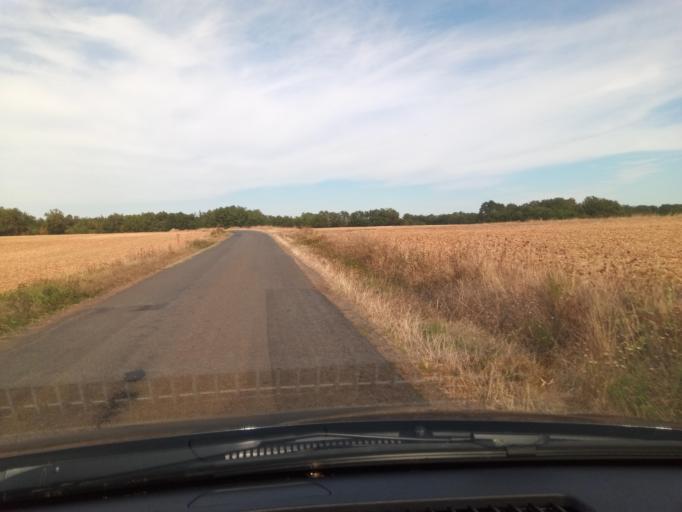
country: FR
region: Poitou-Charentes
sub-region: Departement de la Vienne
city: Chauvigny
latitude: 46.5274
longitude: 0.7343
